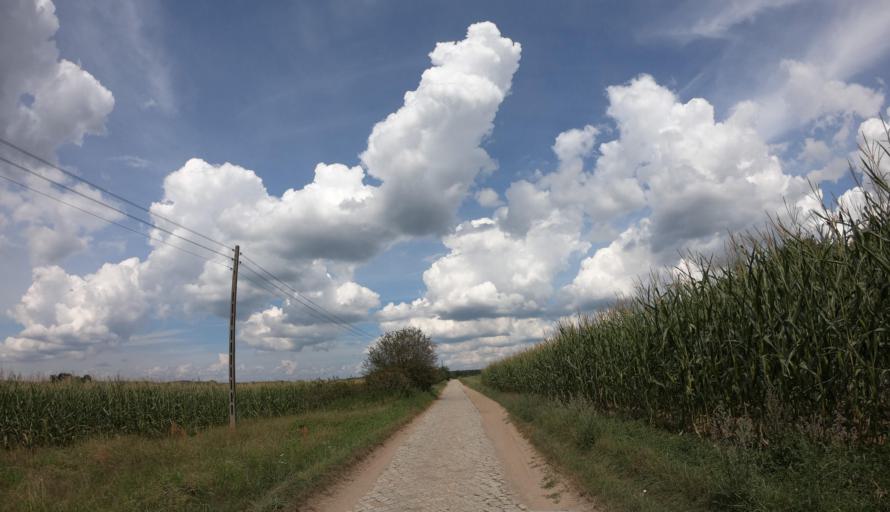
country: PL
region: West Pomeranian Voivodeship
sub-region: Powiat stargardzki
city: Kobylanka
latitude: 53.3174
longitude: 14.8274
